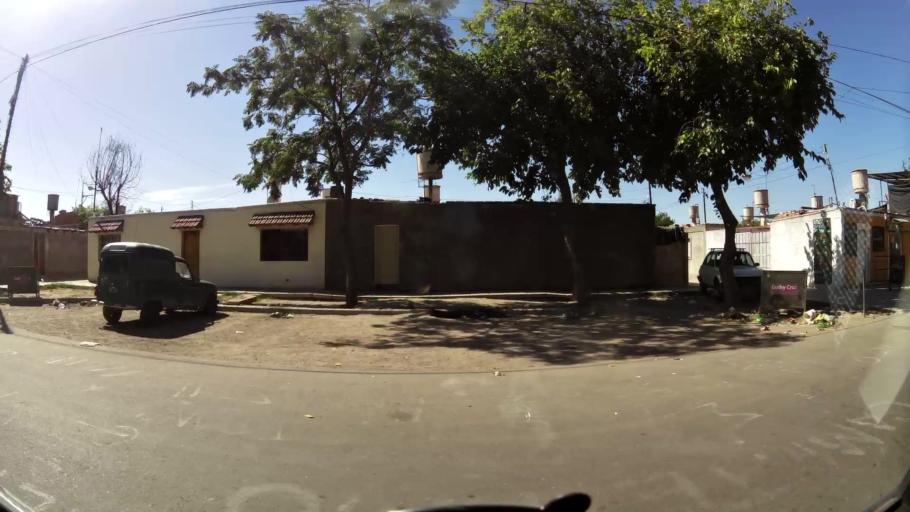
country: AR
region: Mendoza
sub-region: Departamento de Godoy Cruz
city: Godoy Cruz
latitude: -32.9572
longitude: -68.8297
